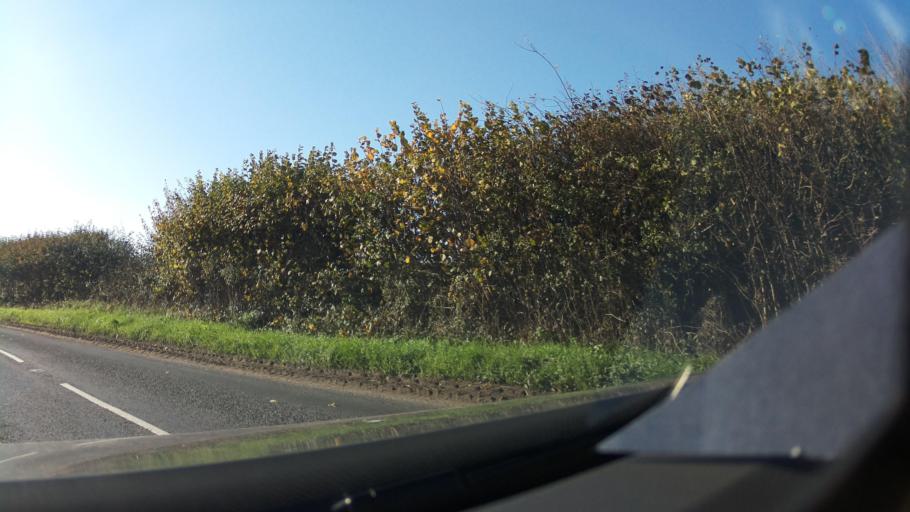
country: GB
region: England
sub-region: Somerset
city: Bruton
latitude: 51.1279
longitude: -2.4353
